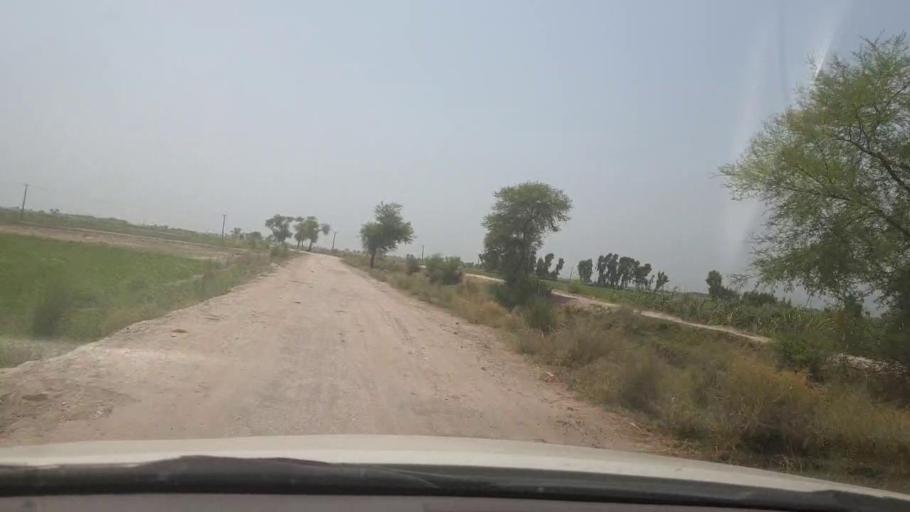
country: PK
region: Sindh
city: Shikarpur
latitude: 28.0512
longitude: 68.5872
